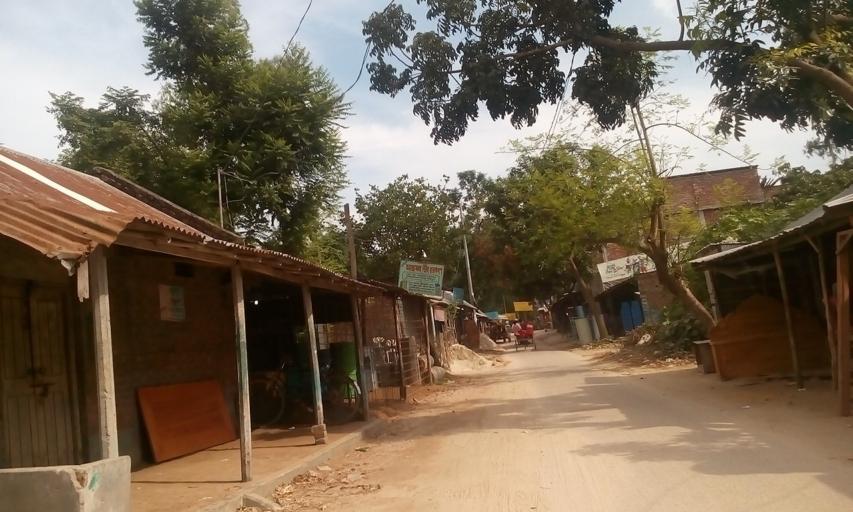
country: IN
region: West Bengal
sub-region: Dakshin Dinajpur
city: Balurghat
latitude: 25.3830
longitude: 88.9864
